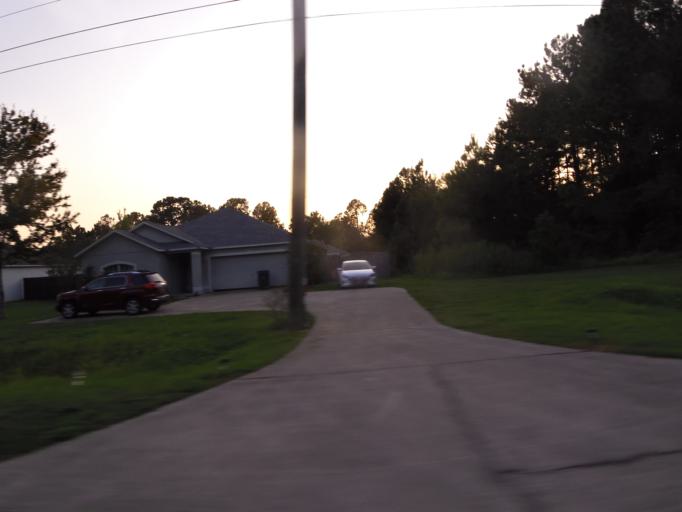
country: US
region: Florida
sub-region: Baker County
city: Macclenny
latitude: 30.2932
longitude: -82.1246
